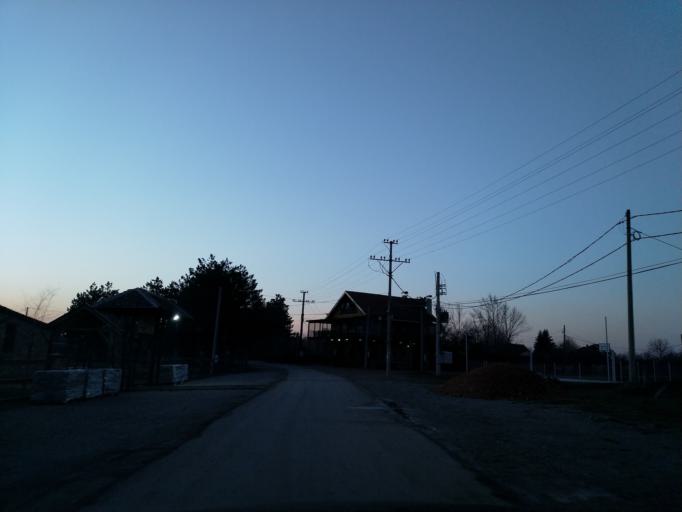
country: RS
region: Central Serbia
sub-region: Pomoravski Okrug
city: Paracin
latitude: 43.8717
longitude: 21.4199
